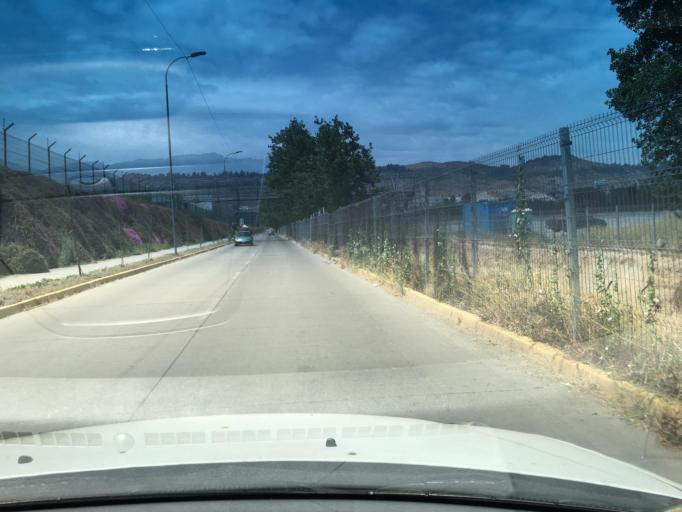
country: CL
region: Santiago Metropolitan
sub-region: Provincia de Santiago
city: Santiago
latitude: -33.3828
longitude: -70.6284
